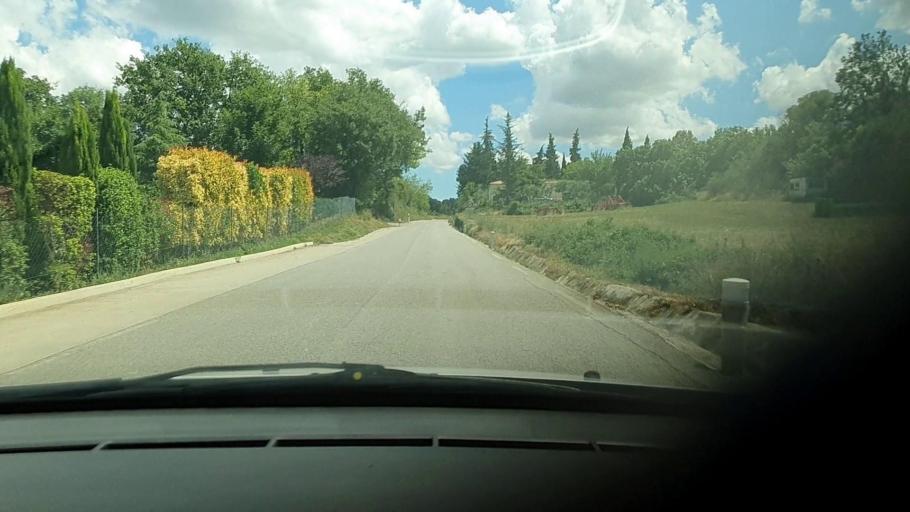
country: FR
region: Languedoc-Roussillon
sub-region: Departement du Gard
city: Moussac
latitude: 44.0537
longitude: 4.2259
